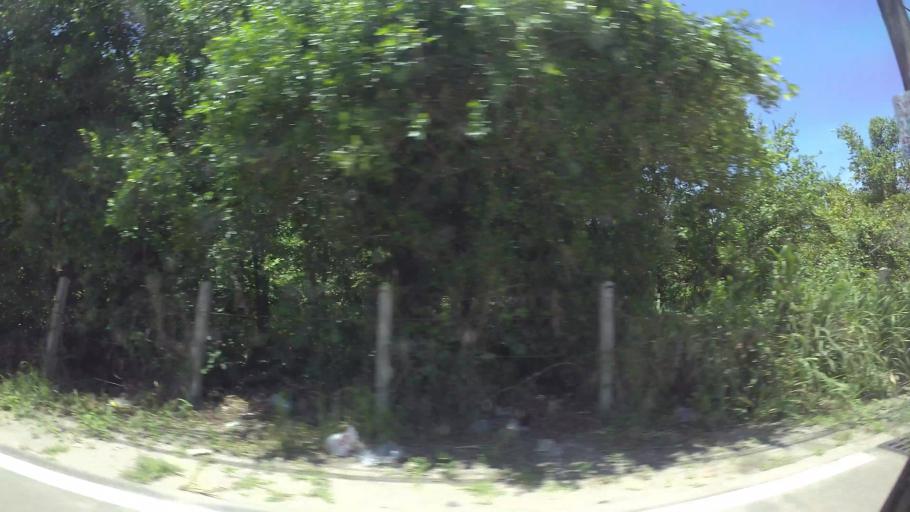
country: TH
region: Chon Buri
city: Si Racha
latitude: 13.1148
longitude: 100.9341
